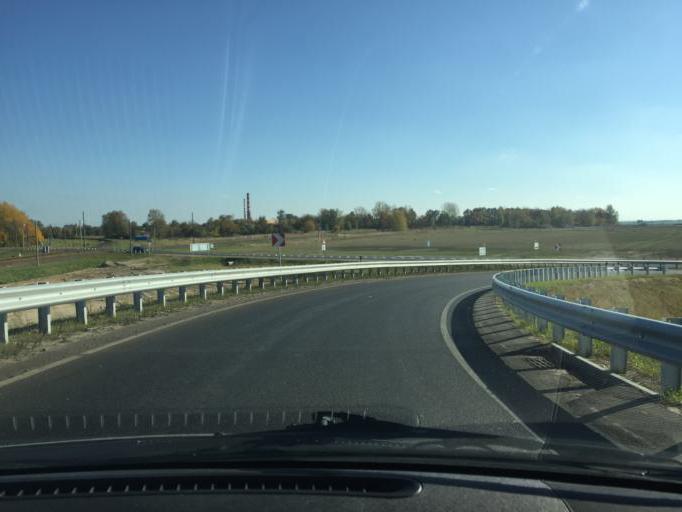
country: BY
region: Minsk
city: Slutsk
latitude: 53.0112
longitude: 27.4881
